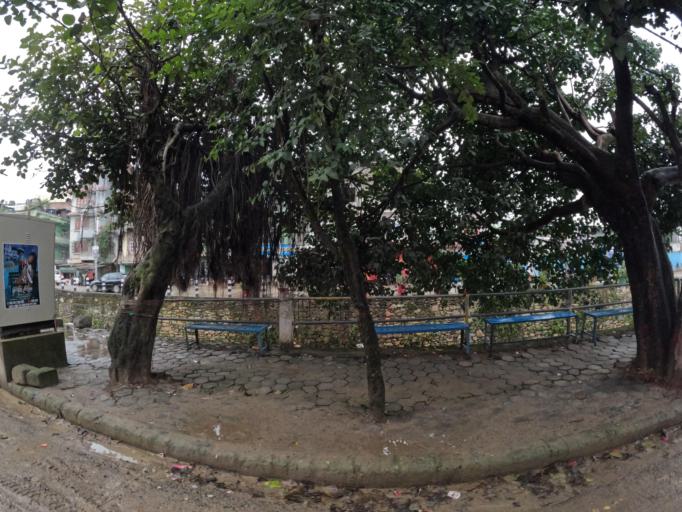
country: NP
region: Central Region
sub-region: Bagmati Zone
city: Kathmandu
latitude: 27.7406
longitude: 85.3126
